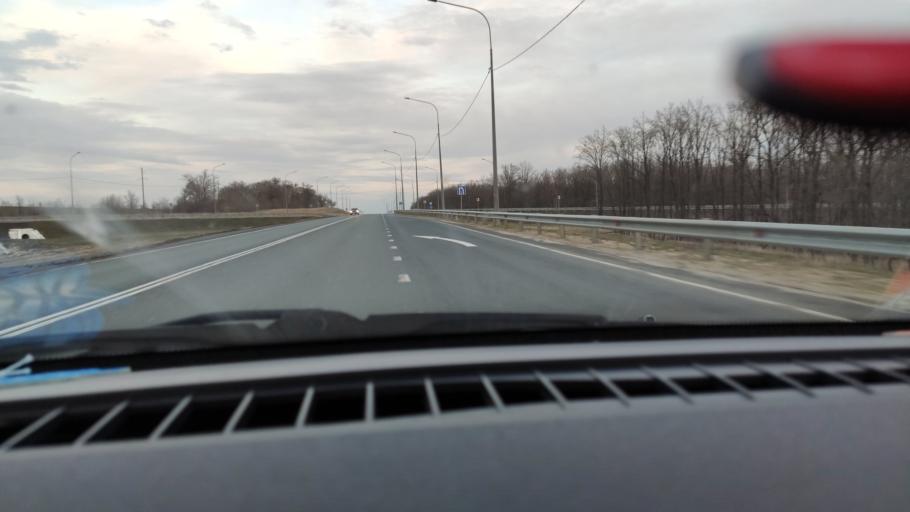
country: RU
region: Saratov
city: Yelshanka
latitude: 51.8243
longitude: 46.3047
